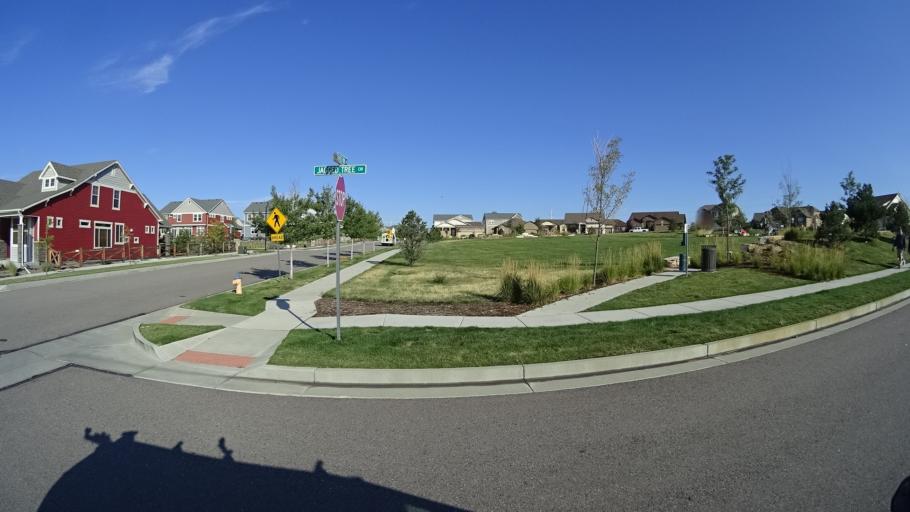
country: US
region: Colorado
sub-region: El Paso County
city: Cimarron Hills
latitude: 38.9342
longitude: -104.6680
